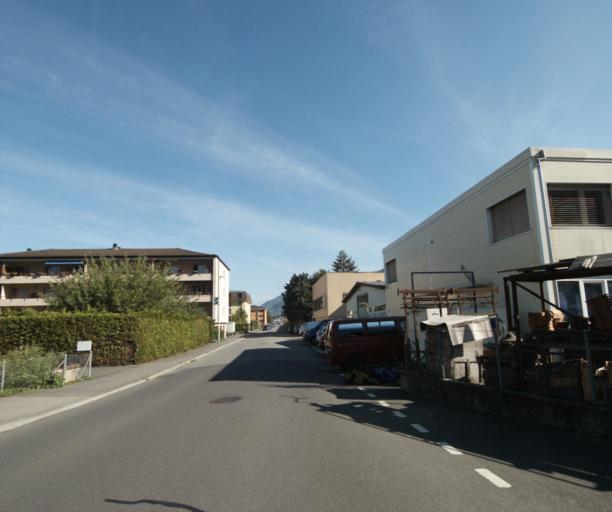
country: CH
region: Vaud
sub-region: Aigle District
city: Villeneuve
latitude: 46.3930
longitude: 6.9298
